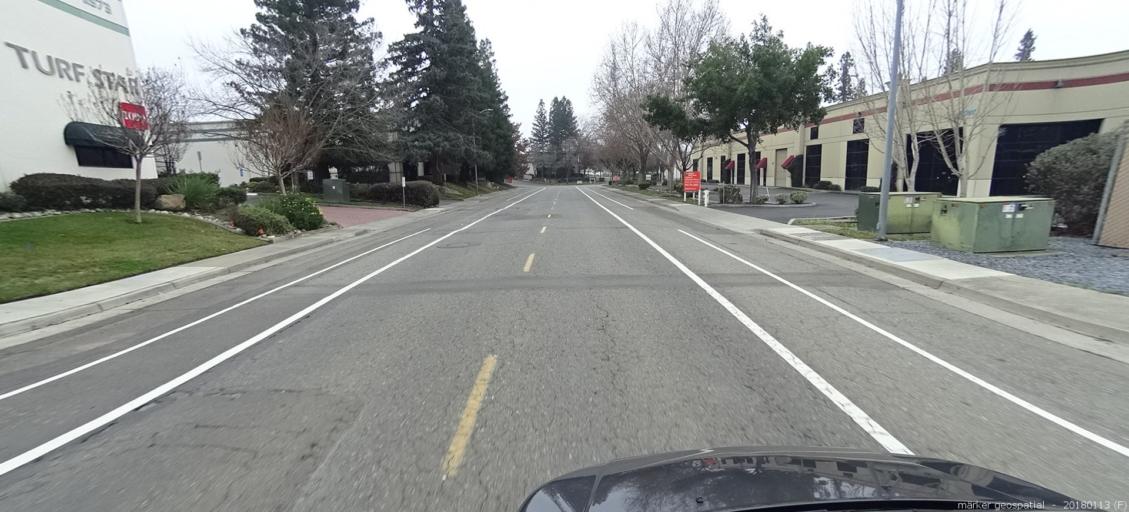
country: US
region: California
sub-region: Sacramento County
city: Gold River
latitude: 38.5988
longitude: -121.2611
